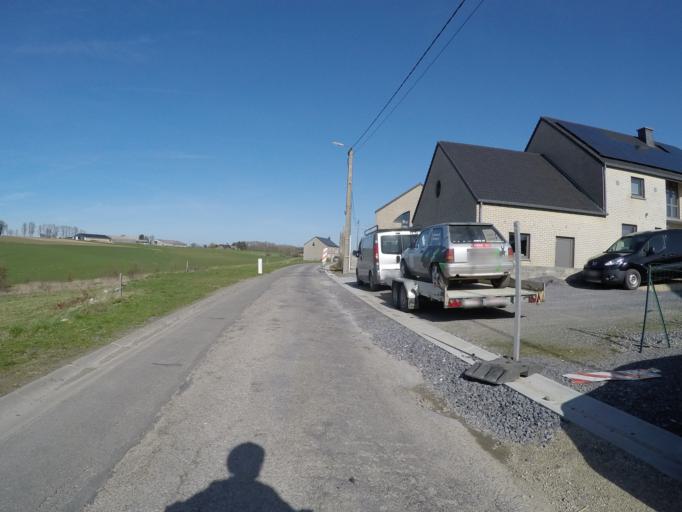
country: BE
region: Wallonia
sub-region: Province de Namur
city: Hamois
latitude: 50.3882
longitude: 5.1546
